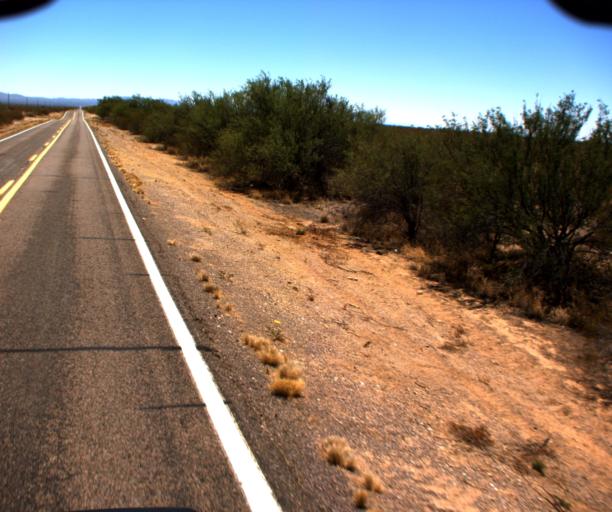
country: US
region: Arizona
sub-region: Pima County
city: Ajo
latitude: 32.2014
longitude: -112.5054
